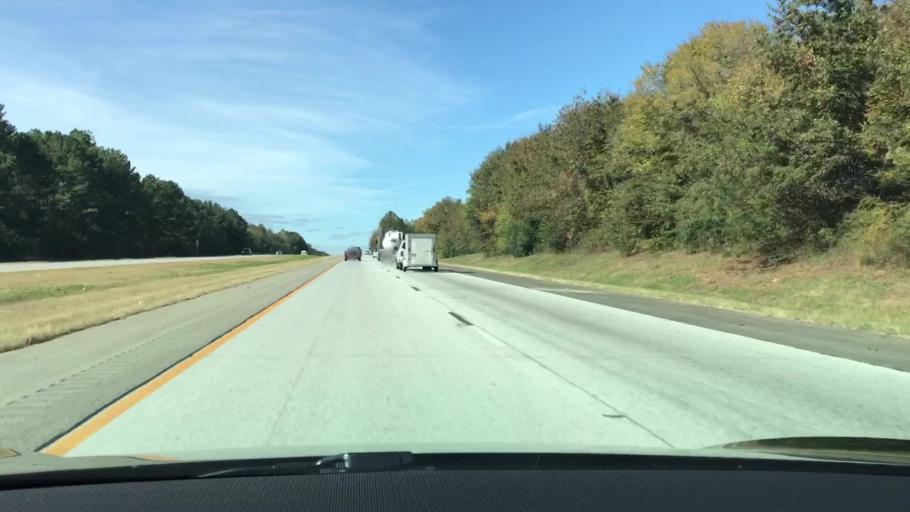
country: US
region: Georgia
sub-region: Morgan County
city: Madison
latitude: 33.5540
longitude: -83.4107
